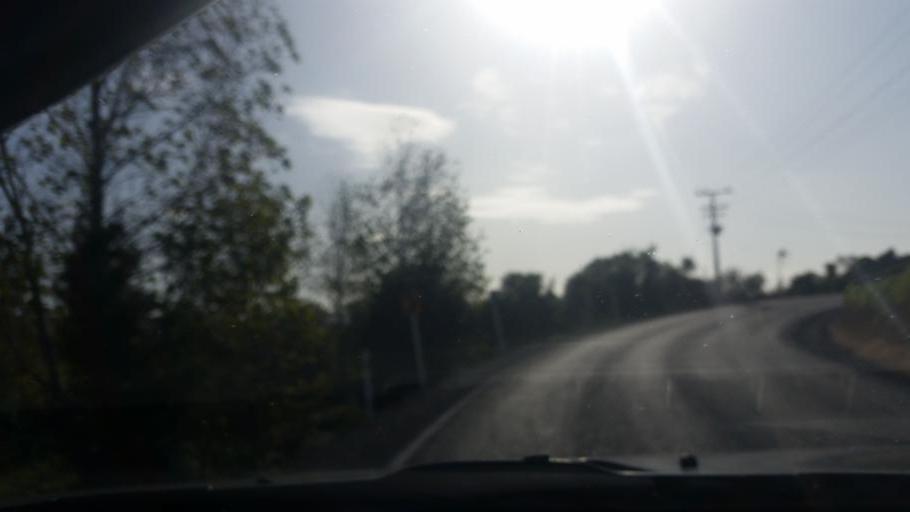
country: NZ
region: Auckland
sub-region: Auckland
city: Wellsford
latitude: -36.1115
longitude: 174.5454
